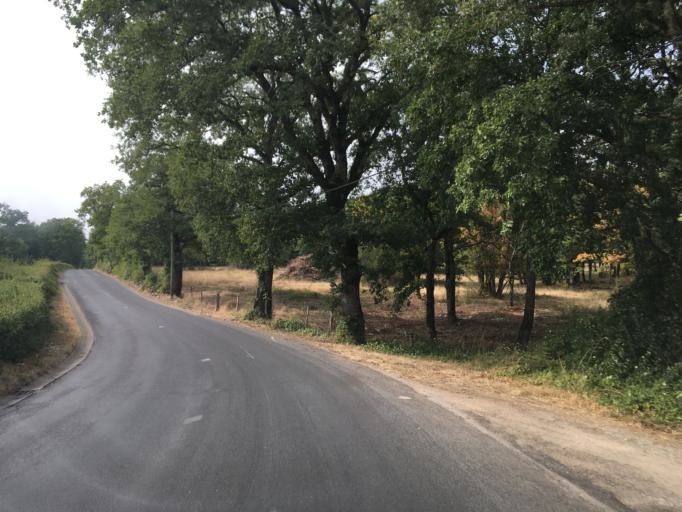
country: FR
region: Midi-Pyrenees
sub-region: Departement du Lot
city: Gramat
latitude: 44.8207
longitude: 1.6042
